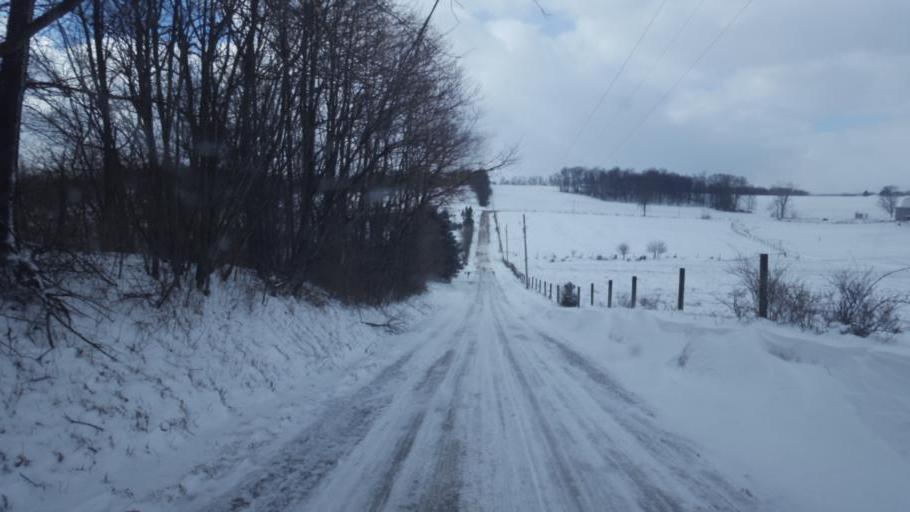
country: US
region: Ohio
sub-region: Knox County
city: Gambier
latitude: 40.5187
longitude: -82.3857
